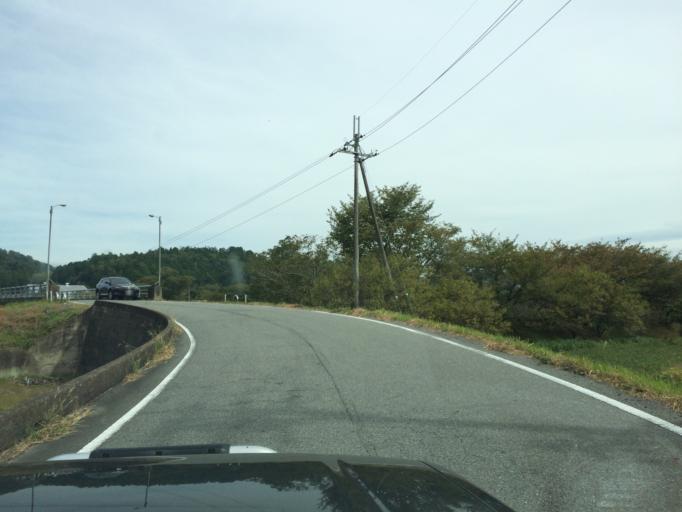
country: JP
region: Hyogo
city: Sasayama
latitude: 35.0718
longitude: 135.2607
